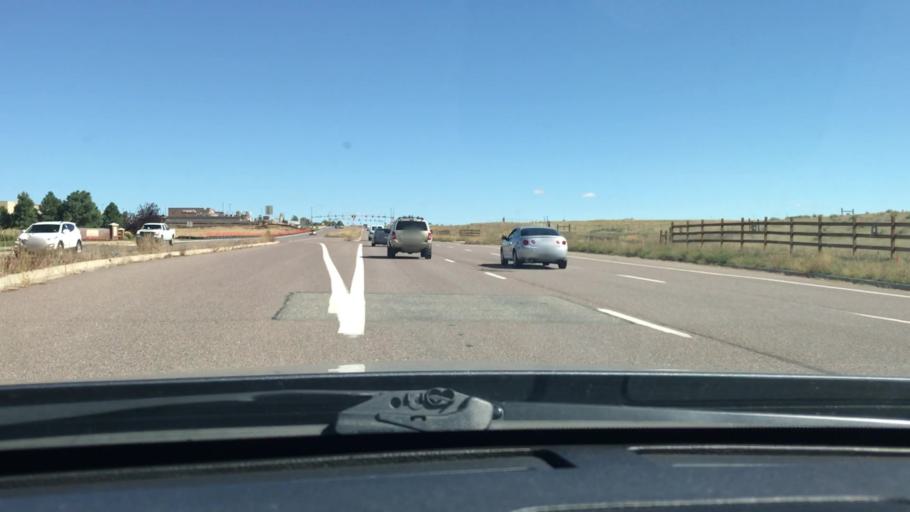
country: US
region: Colorado
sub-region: Arapahoe County
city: Dove Valley
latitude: 39.6384
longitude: -104.7431
